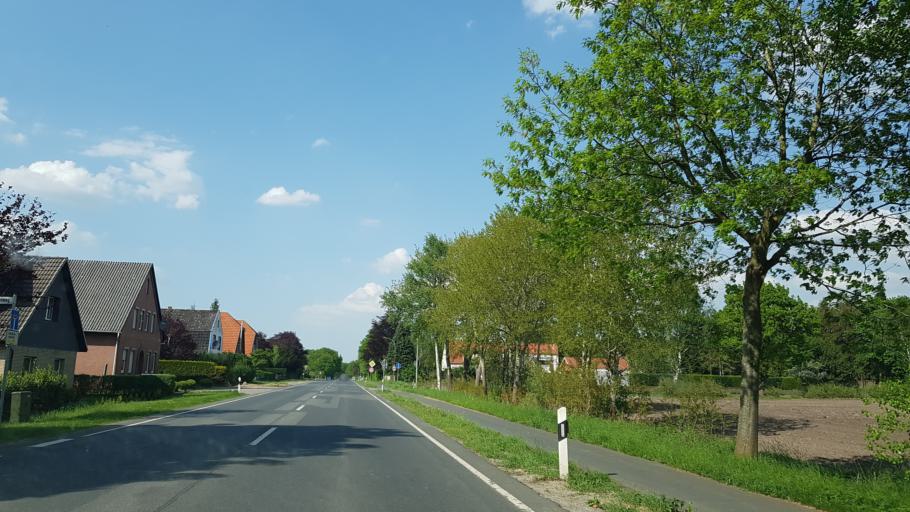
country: DE
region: Lower Saxony
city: Langen
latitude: 53.6260
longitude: 8.6006
